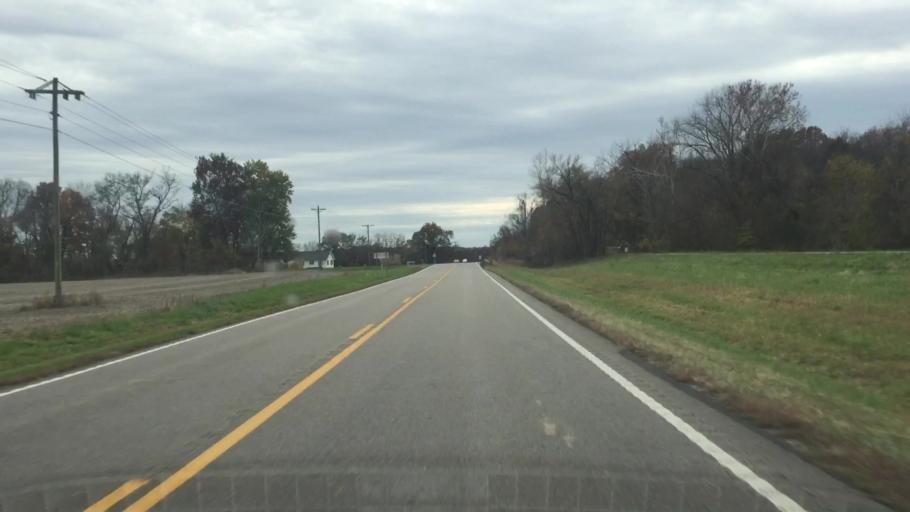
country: US
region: Missouri
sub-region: Callaway County
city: Holts Summit
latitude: 38.6042
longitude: -91.9926
